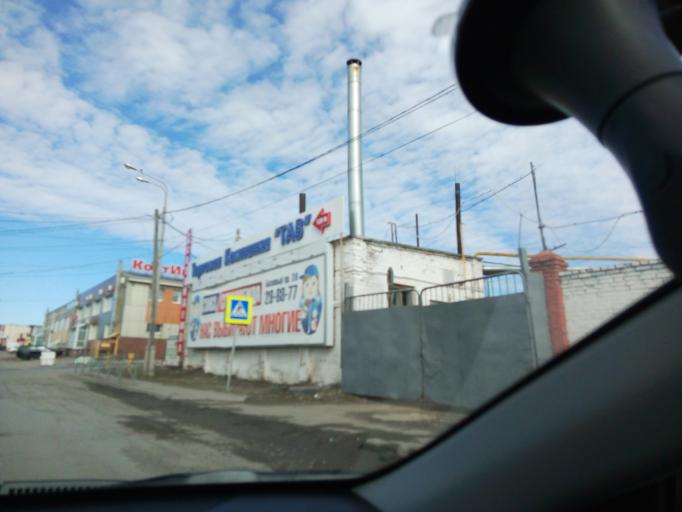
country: RU
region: Chuvashia
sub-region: Cheboksarskiy Rayon
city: Cheboksary
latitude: 56.1046
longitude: 47.2520
